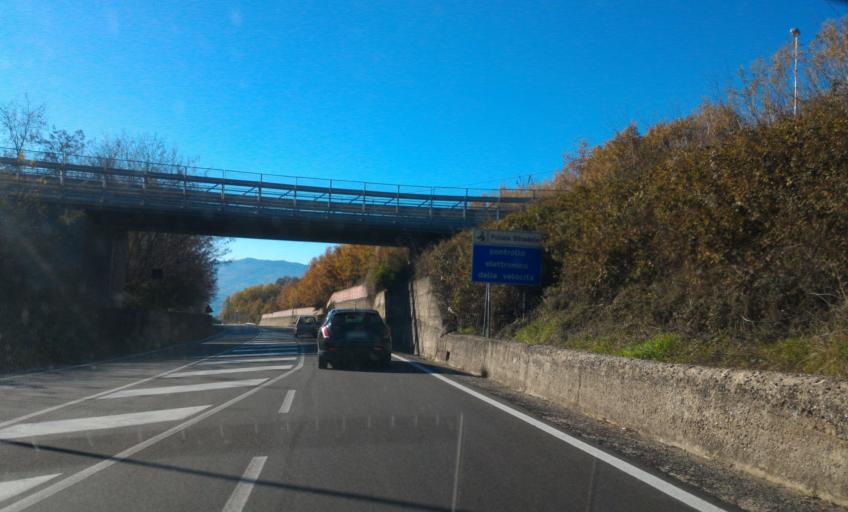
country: IT
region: Calabria
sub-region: Provincia di Cosenza
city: Rovito
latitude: 39.3094
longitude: 16.3258
